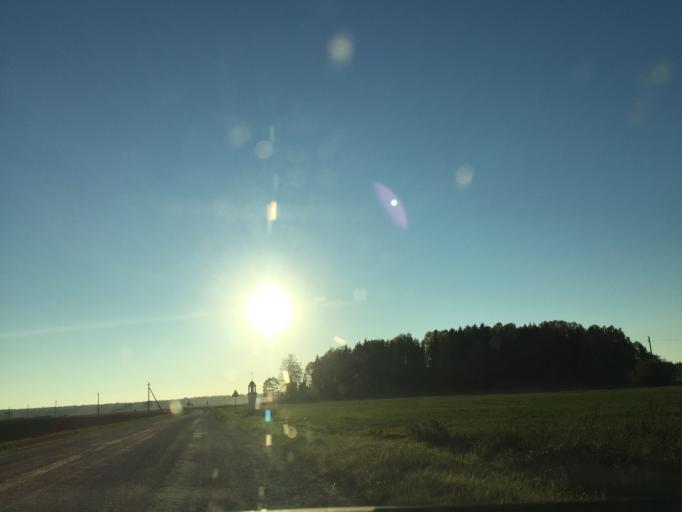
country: LT
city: Vieksniai
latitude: 56.3092
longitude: 22.5448
